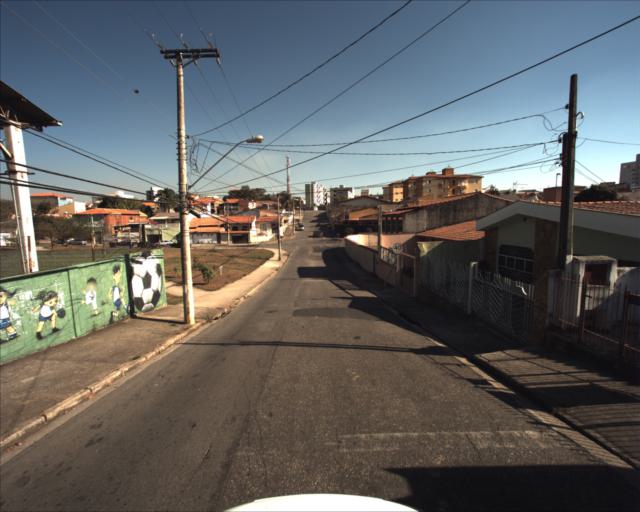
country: BR
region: Sao Paulo
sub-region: Sorocaba
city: Sorocaba
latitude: -23.5069
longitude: -47.4250
